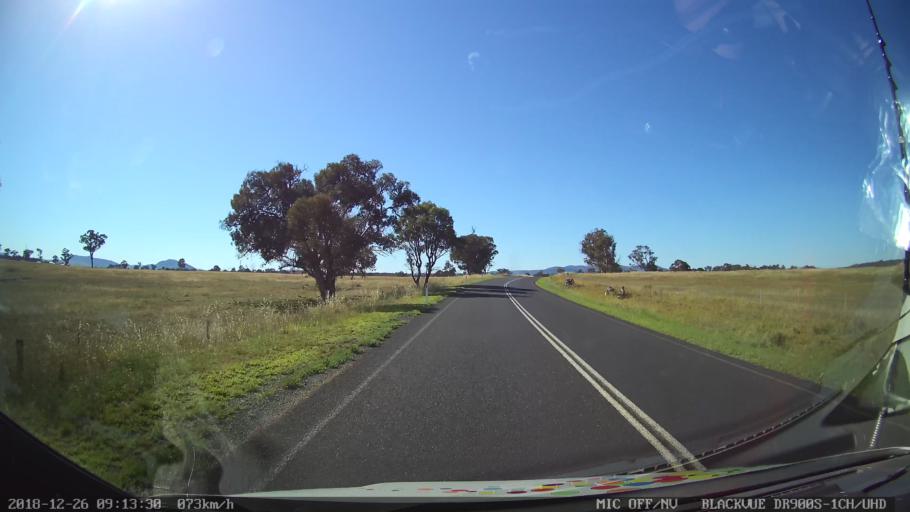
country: AU
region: New South Wales
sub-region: Mid-Western Regional
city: Kandos
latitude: -32.7682
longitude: 149.9800
